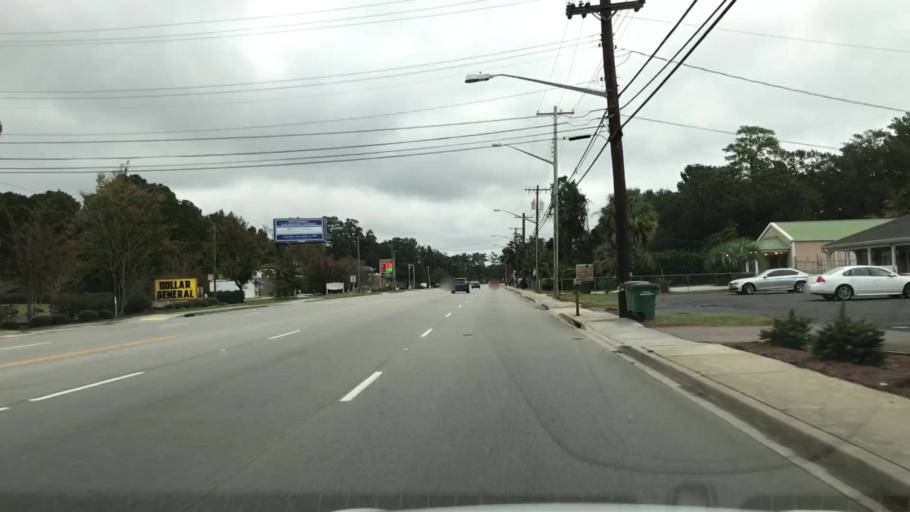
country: US
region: South Carolina
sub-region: Georgetown County
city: Georgetown
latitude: 33.3467
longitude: -79.2962
